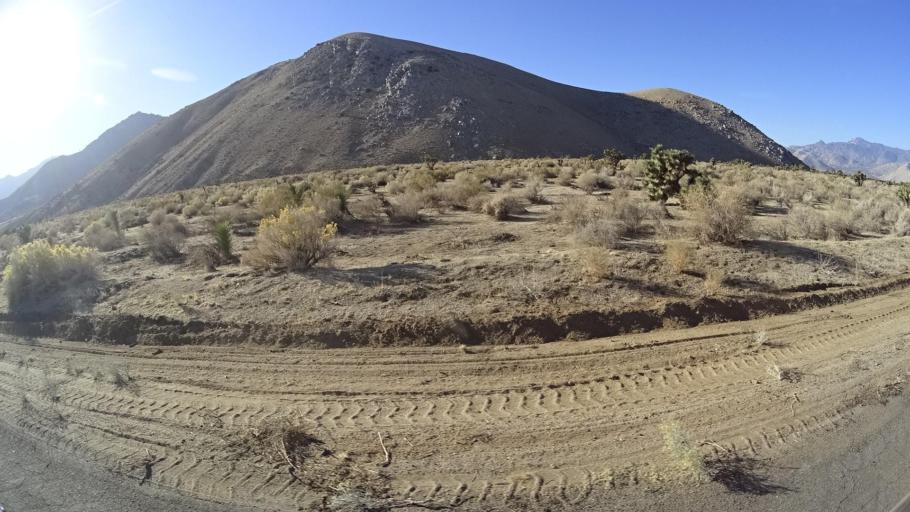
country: US
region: California
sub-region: Kern County
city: Weldon
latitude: 35.6071
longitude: -118.2435
